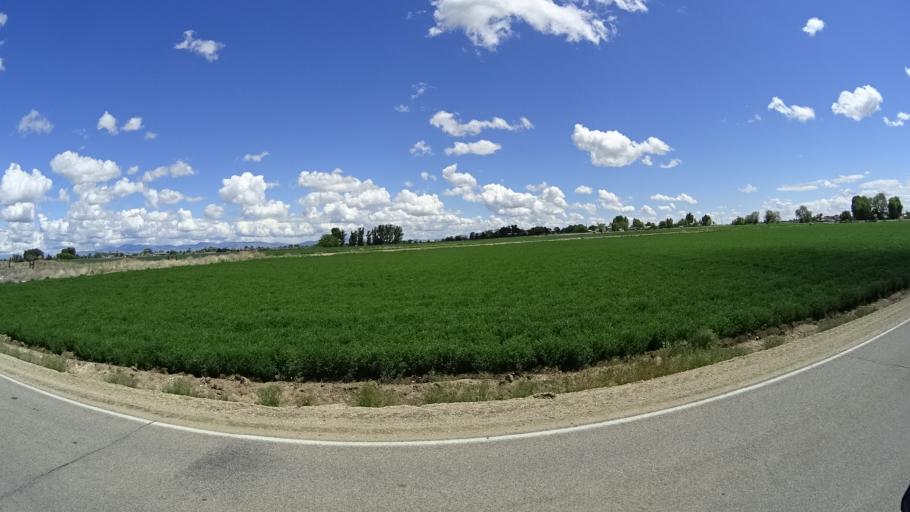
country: US
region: Idaho
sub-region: Ada County
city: Kuna
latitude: 43.5494
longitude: -116.4538
